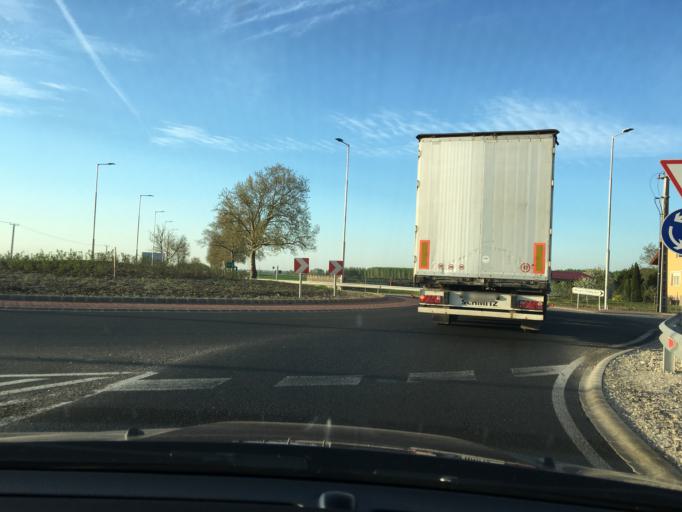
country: HU
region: Hajdu-Bihar
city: Mikepercs
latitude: 47.4623
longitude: 21.6363
